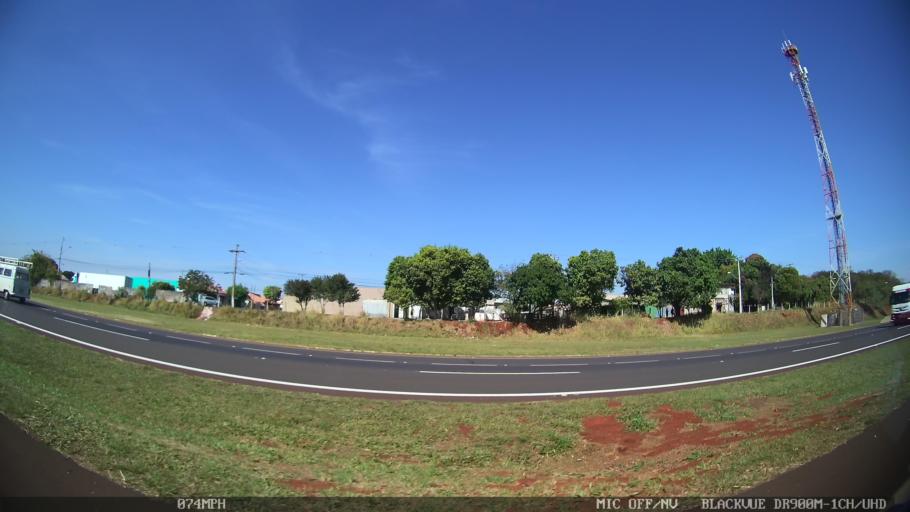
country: BR
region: Sao Paulo
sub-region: Ribeirao Preto
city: Ribeirao Preto
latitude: -21.1040
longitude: -47.8057
